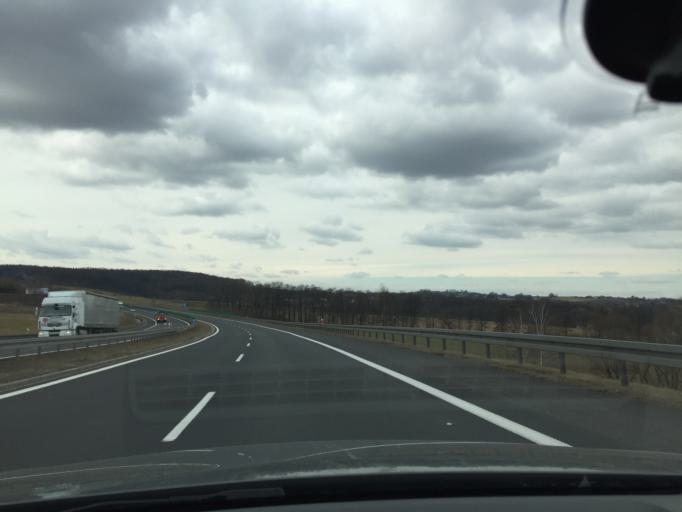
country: PL
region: Silesian Voivodeship
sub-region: Powiat cieszynski
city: Debowiec
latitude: 49.7787
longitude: 18.7310
